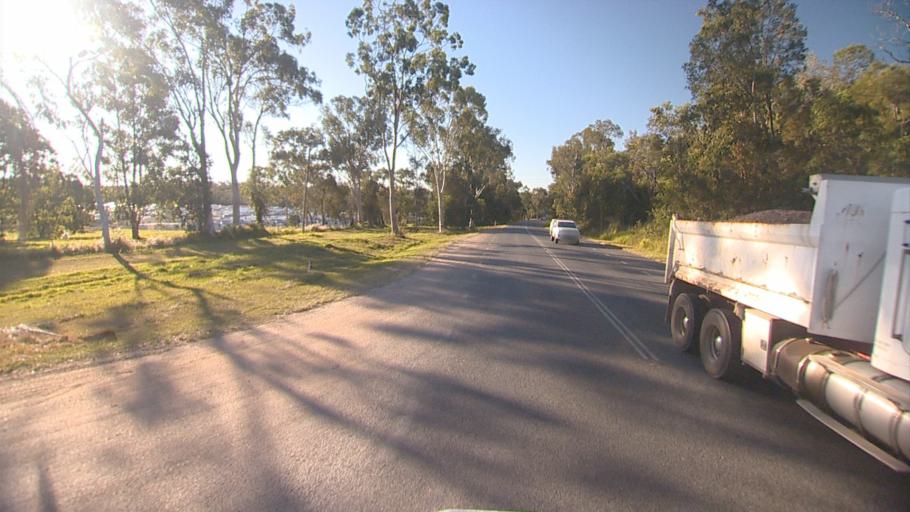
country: AU
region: Queensland
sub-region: Logan
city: Logan Reserve
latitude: -27.7254
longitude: 153.0901
